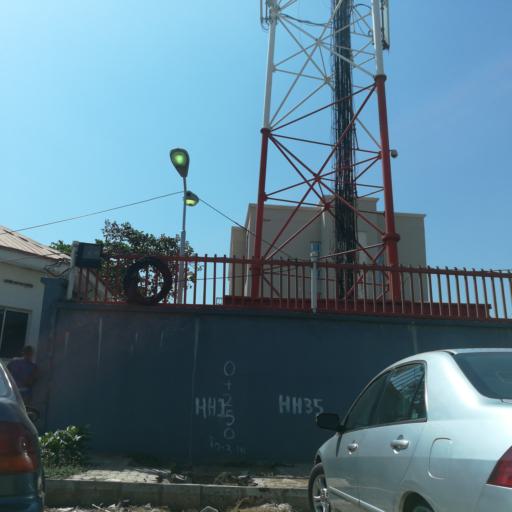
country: NG
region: Kano
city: Kano
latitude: 12.0061
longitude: 8.5395
